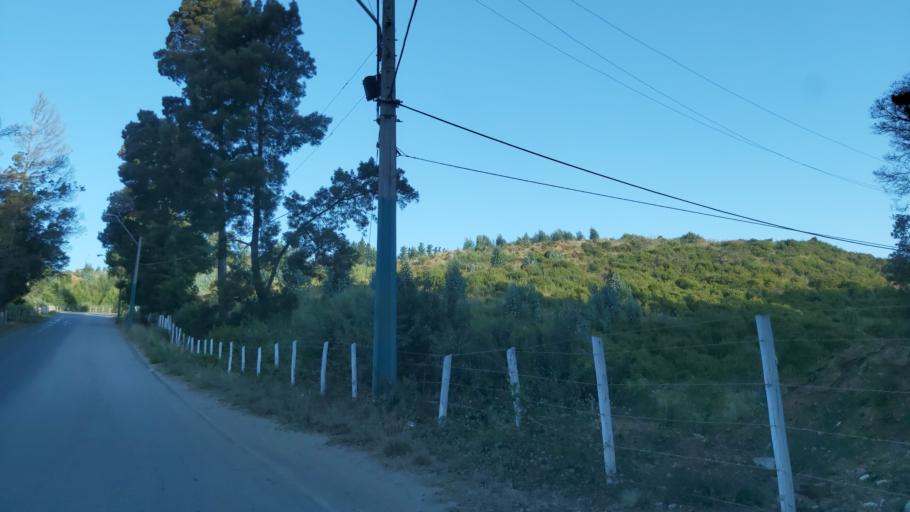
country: CL
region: Biobio
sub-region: Provincia de Concepcion
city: Tome
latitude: -36.5350
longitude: -72.9302
